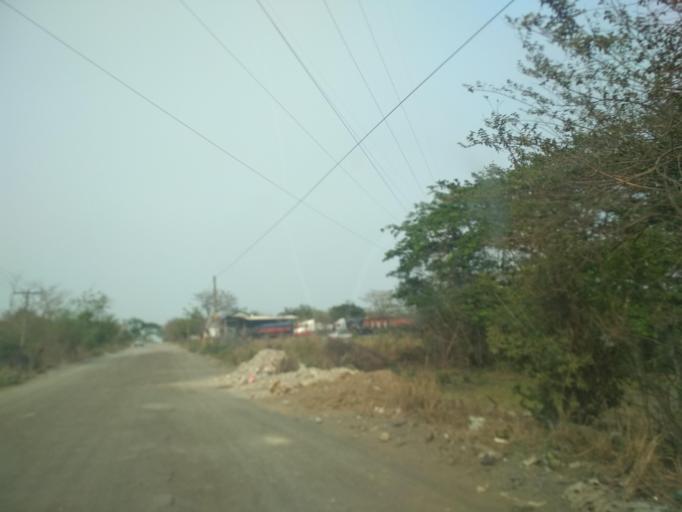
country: MX
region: Veracruz
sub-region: Veracruz
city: Las Amapolas
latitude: 19.1469
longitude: -96.2384
